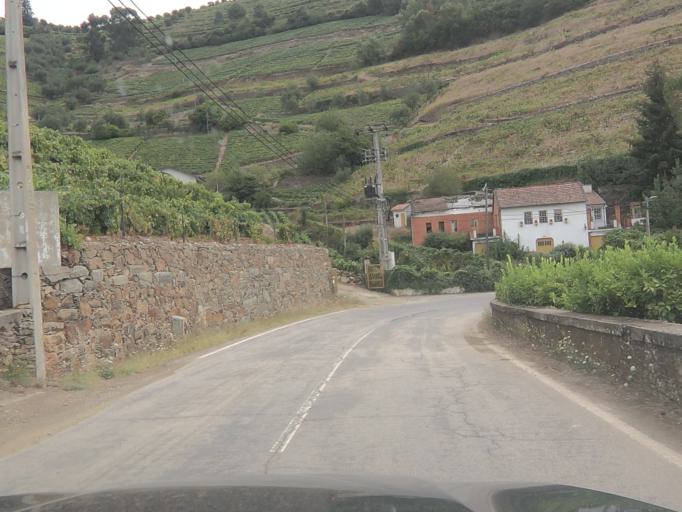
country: PT
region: Vila Real
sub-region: Santa Marta de Penaguiao
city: Santa Marta de Penaguiao
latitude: 41.2293
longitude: -7.7661
